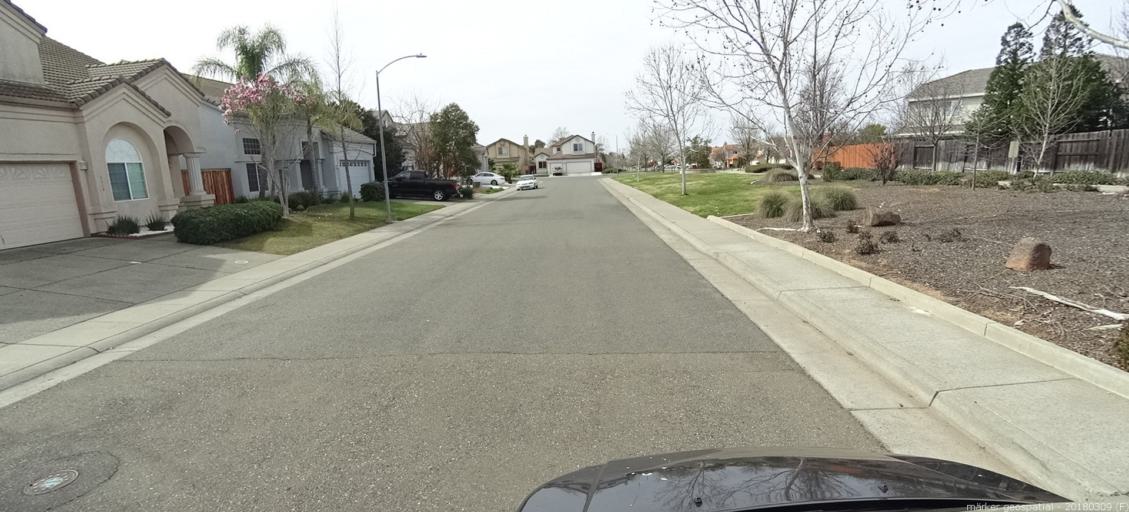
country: US
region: California
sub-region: Sacramento County
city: Vineyard
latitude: 38.4597
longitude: -121.3661
